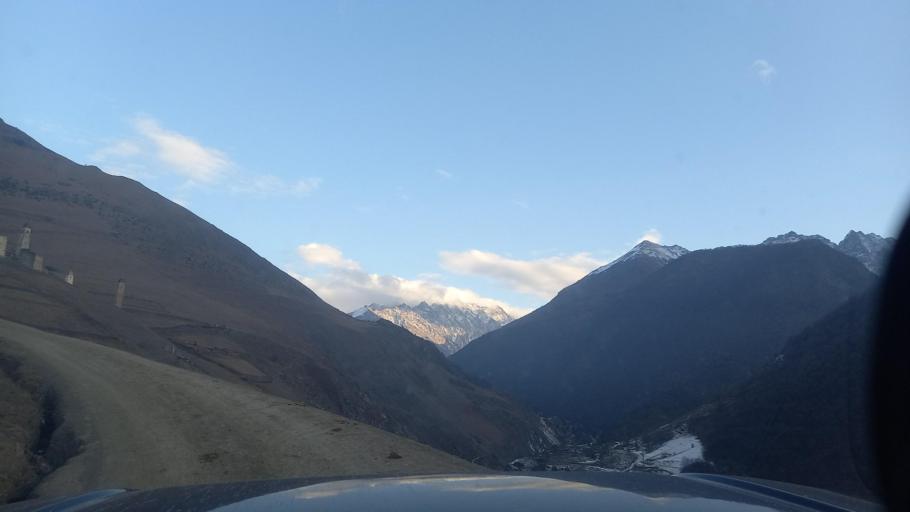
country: RU
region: Ingushetiya
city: Dzhayrakh
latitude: 42.8040
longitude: 44.7534
